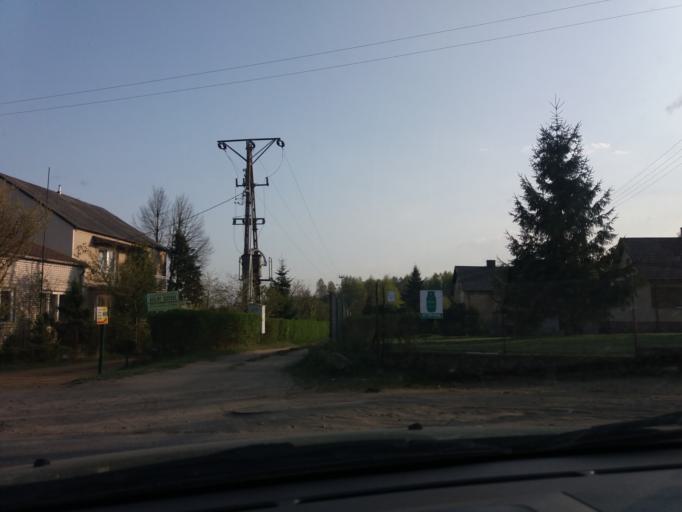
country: PL
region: Masovian Voivodeship
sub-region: Powiat mlawski
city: Mlawa
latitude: 53.1256
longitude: 20.3433
